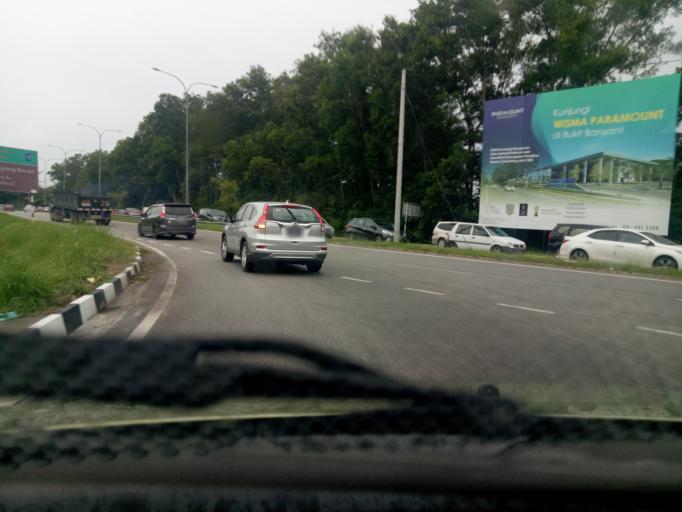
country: MY
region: Kedah
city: Sungai Petani
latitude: 5.6694
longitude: 100.5071
